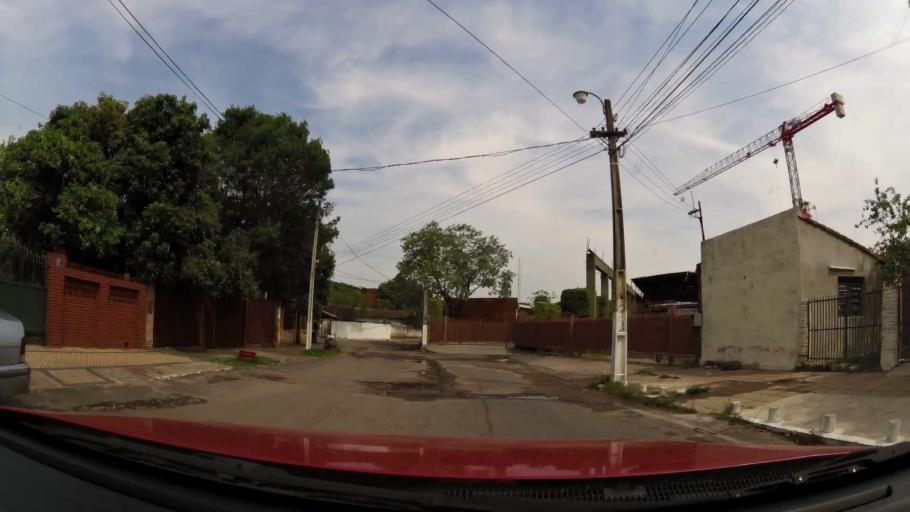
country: PY
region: Asuncion
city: Asuncion
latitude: -25.2631
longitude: -57.5847
